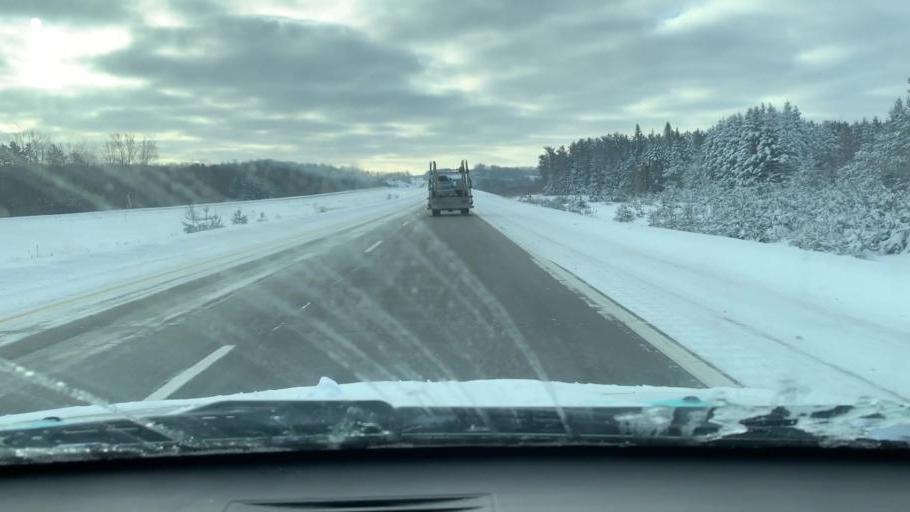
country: US
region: Michigan
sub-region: Wexford County
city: Manton
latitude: 44.4338
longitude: -85.3922
